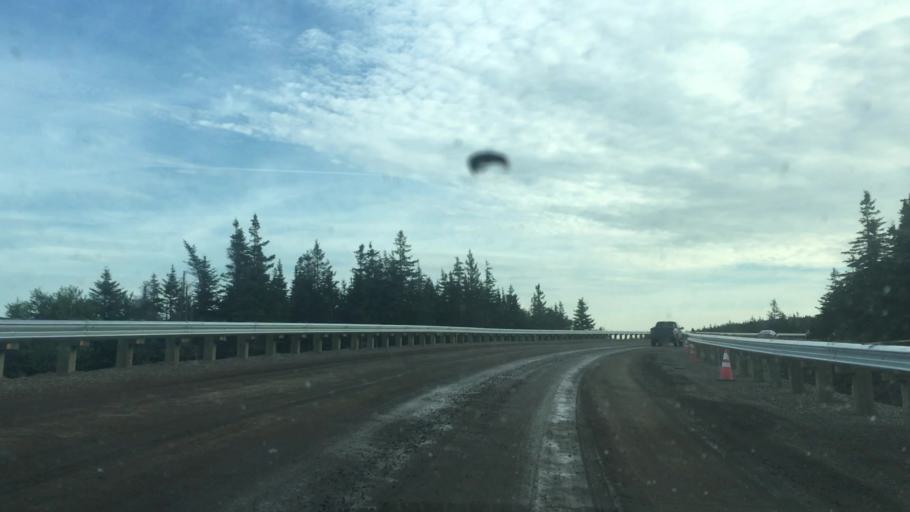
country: CA
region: Nova Scotia
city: Sydney Mines
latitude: 46.8094
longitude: -60.8420
